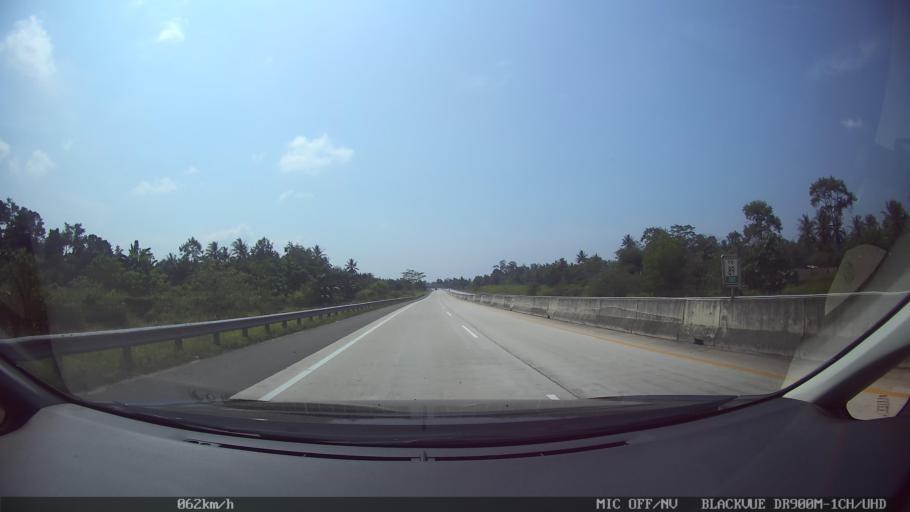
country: ID
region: Lampung
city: Natar
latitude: -5.3113
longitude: 105.2541
